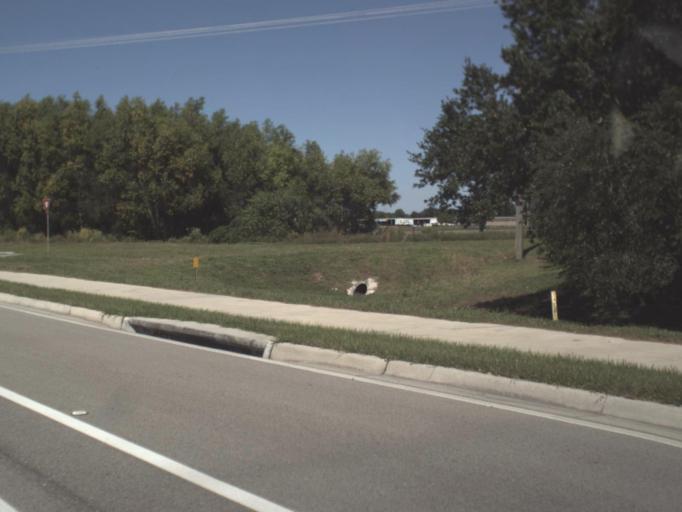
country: US
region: Florida
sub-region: Lee County
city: San Carlos Park
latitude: 26.4919
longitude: -81.8453
